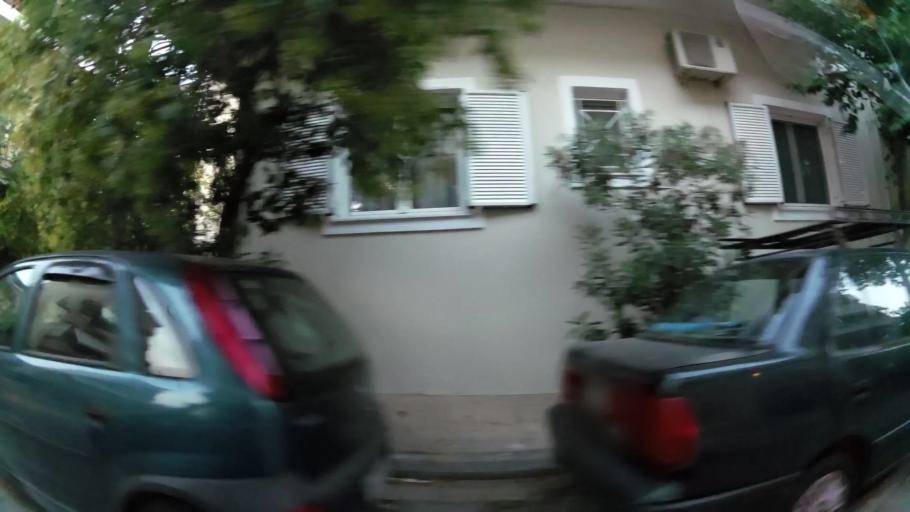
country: GR
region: Attica
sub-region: Nomarchia Athinas
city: Ilion
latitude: 38.0324
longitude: 23.6927
